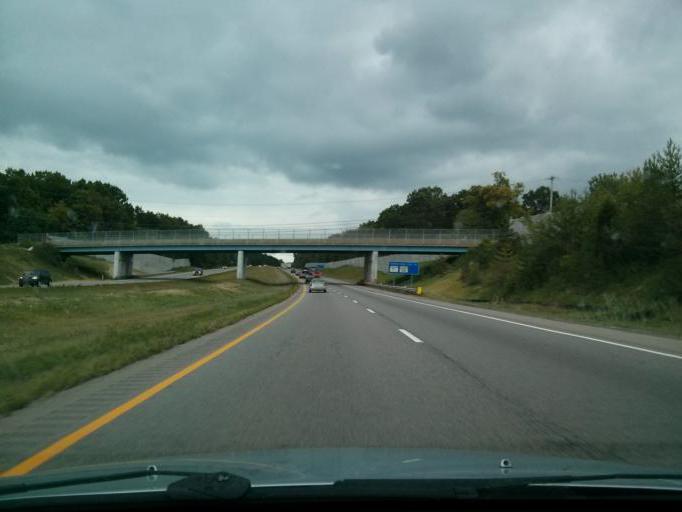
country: US
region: Ohio
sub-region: Mahoning County
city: Craig Beach
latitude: 41.1005
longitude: -80.9727
